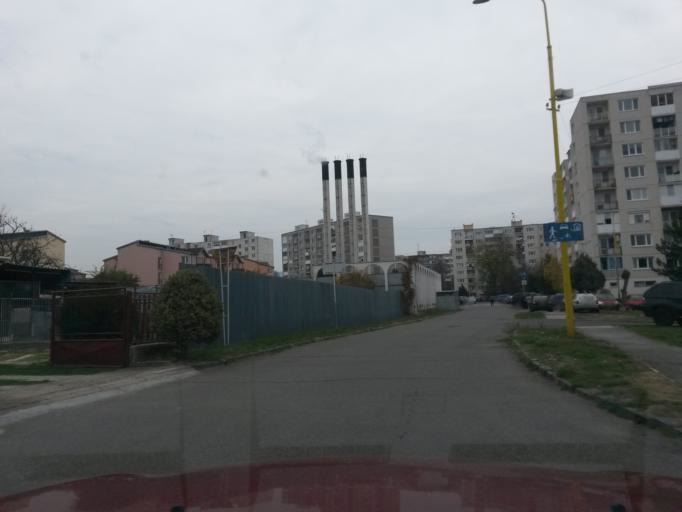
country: SK
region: Kosicky
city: Secovce
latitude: 48.6987
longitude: 21.6571
